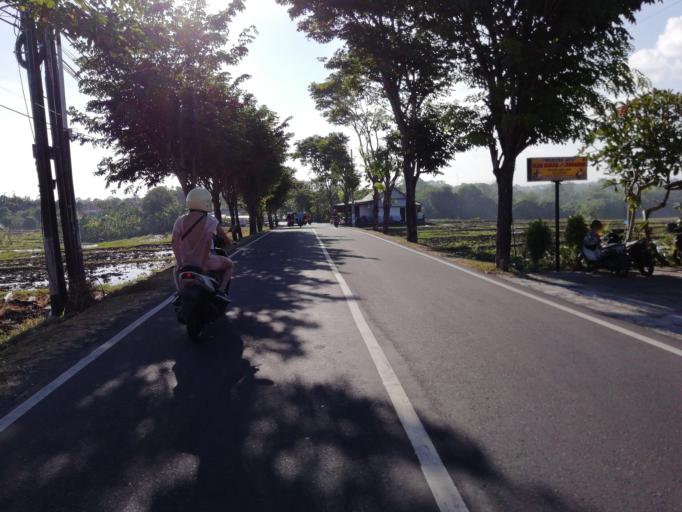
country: ID
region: Bali
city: Banjar Kerobokan
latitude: -8.6337
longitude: 115.1379
